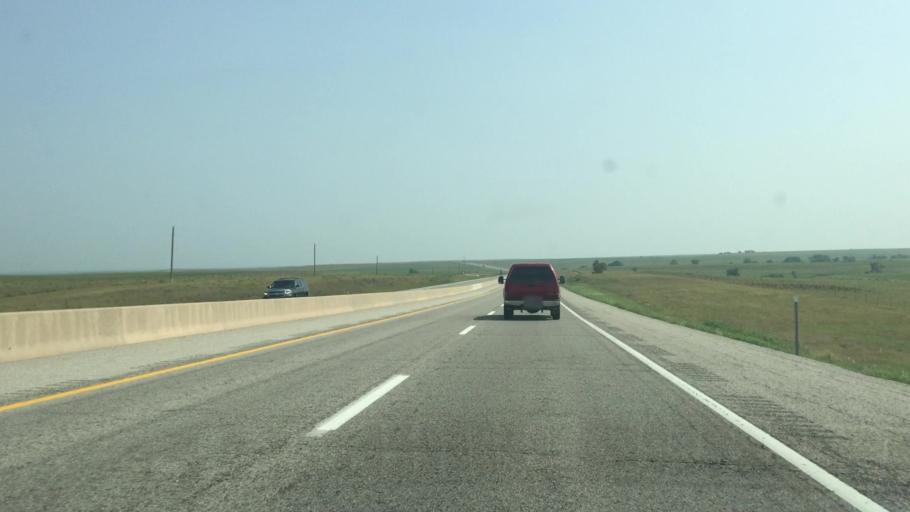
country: US
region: Kansas
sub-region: Chase County
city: Cottonwood Falls
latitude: 38.2799
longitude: -96.3689
